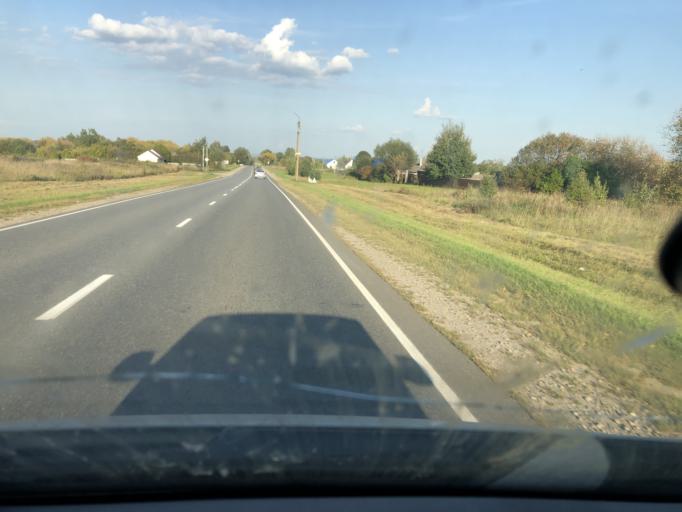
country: RU
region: Kaluga
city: Sosenskiy
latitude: 54.2104
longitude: 35.9813
